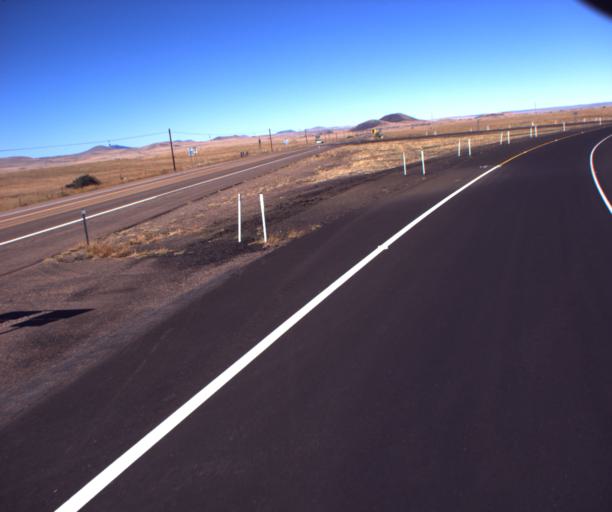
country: US
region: Arizona
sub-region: Apache County
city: Springerville
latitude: 34.1730
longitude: -109.3168
